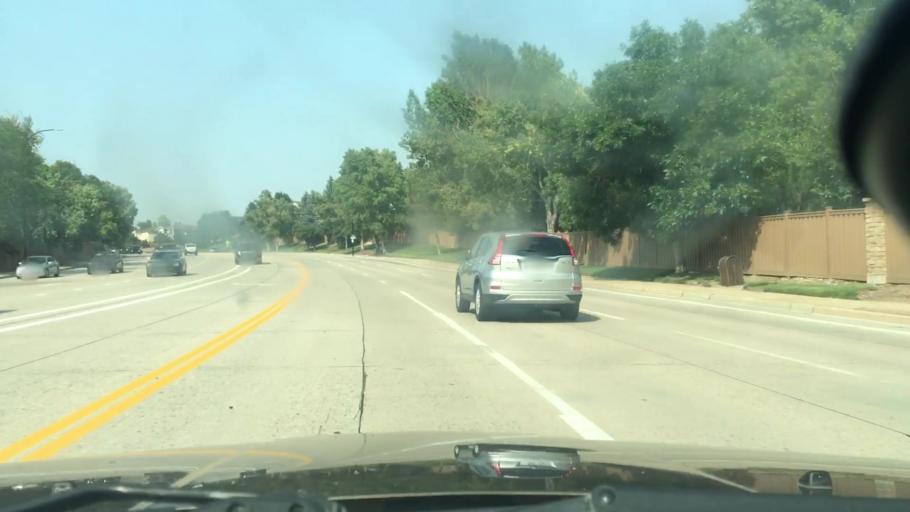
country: US
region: Colorado
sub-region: Douglas County
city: Carriage Club
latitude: 39.5438
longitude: -104.9113
